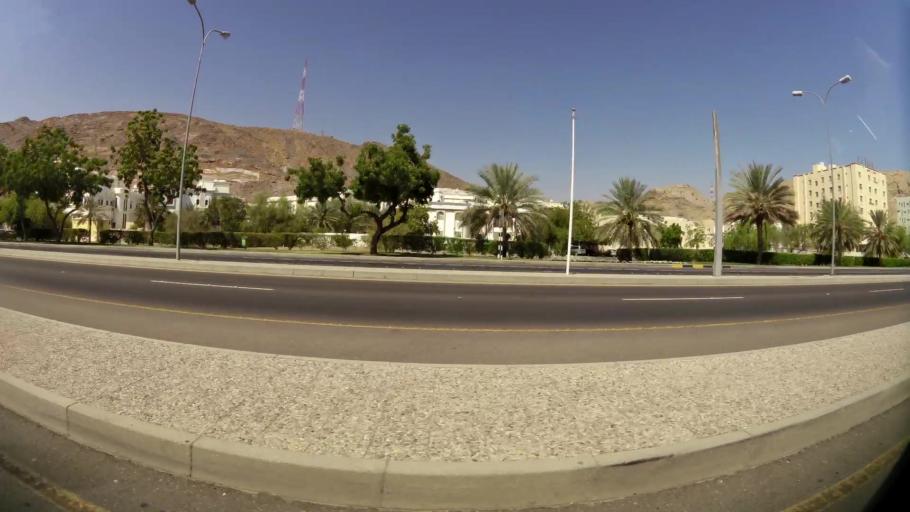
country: OM
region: Muhafazat Masqat
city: Muscat
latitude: 23.5977
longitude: 58.5391
